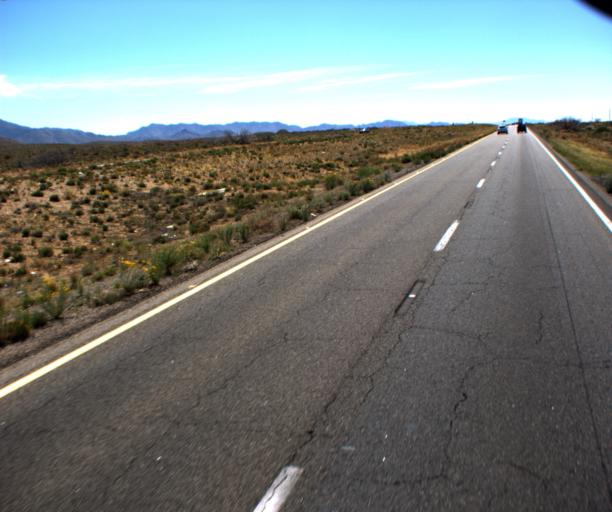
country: US
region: Arizona
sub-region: Mohave County
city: Dolan Springs
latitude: 35.4237
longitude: -114.2790
